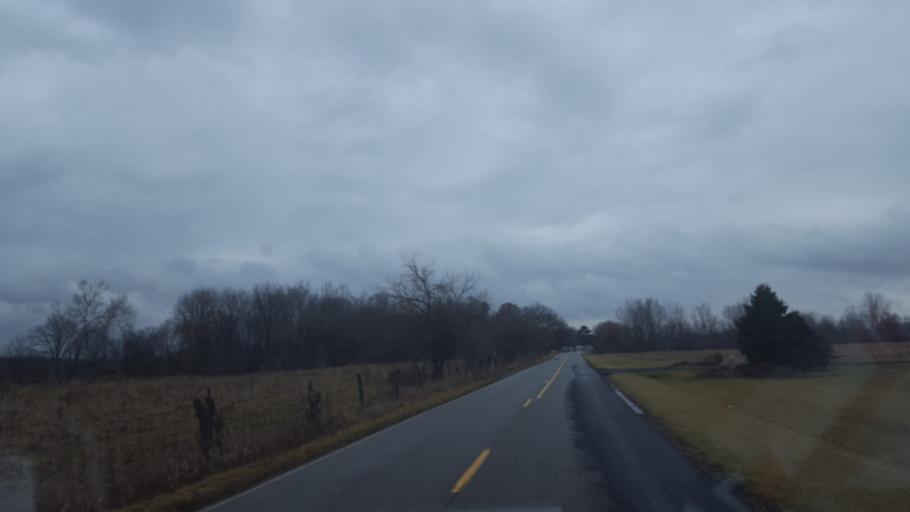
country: US
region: Ohio
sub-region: Knox County
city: Mount Vernon
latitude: 40.4307
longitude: -82.5043
